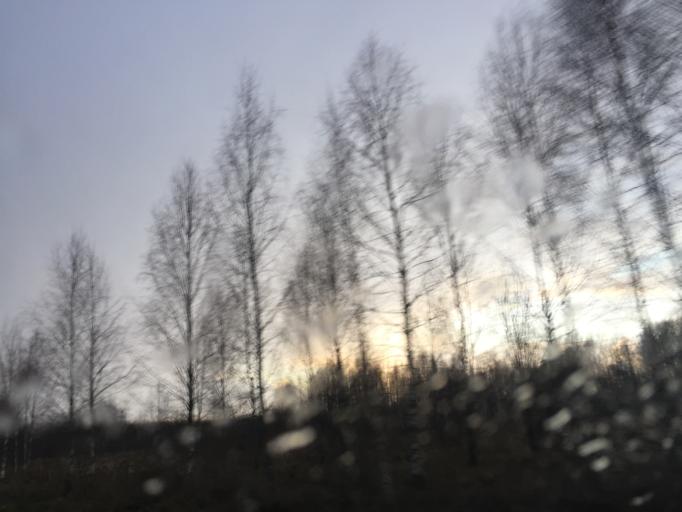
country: LV
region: Burtnieki
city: Matisi
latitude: 57.6846
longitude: 25.2461
